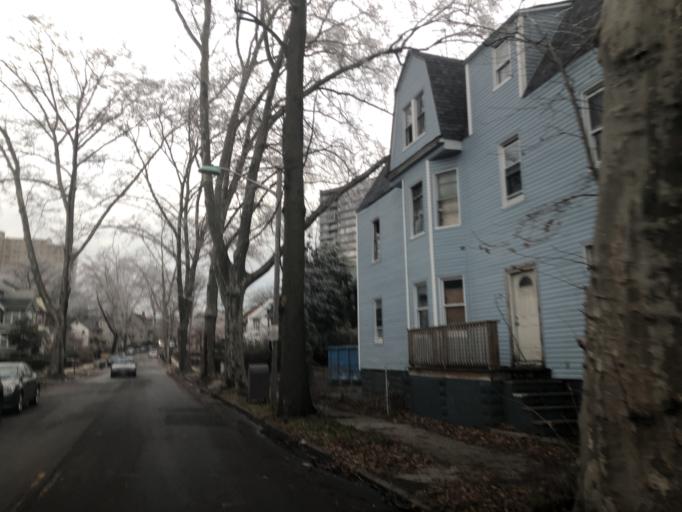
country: US
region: New Jersey
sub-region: Essex County
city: Orange
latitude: 40.7576
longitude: -74.2270
